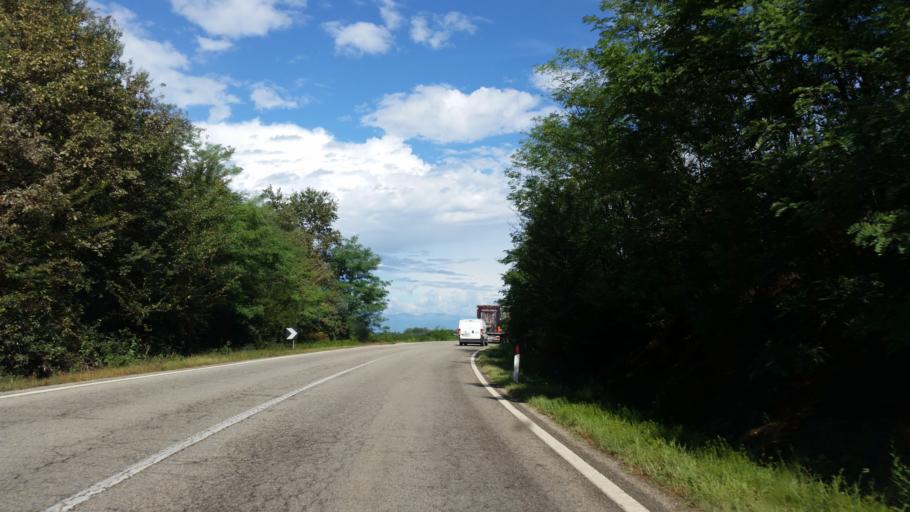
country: IT
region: Piedmont
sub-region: Provincia di Cuneo
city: Monta
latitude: 44.8308
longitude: 7.9271
